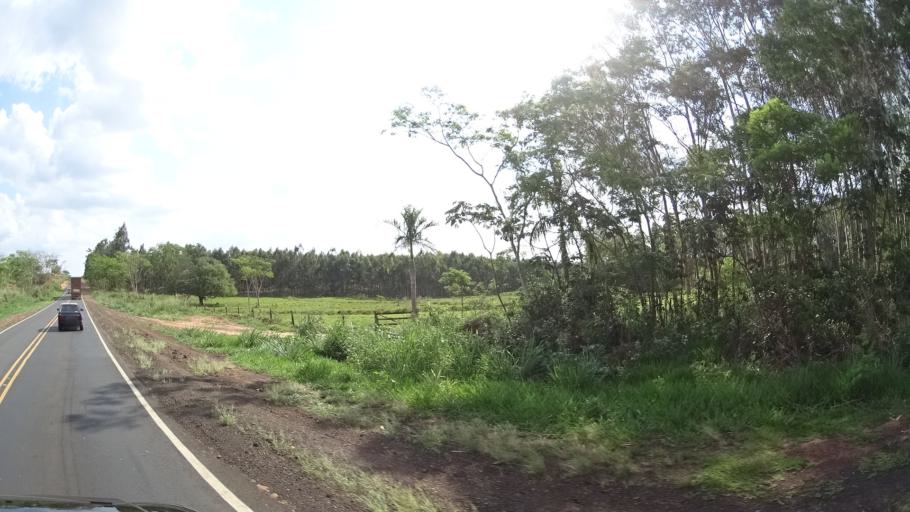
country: BR
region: Sao Paulo
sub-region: Urupes
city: Urupes
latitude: -21.1671
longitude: -49.2885
